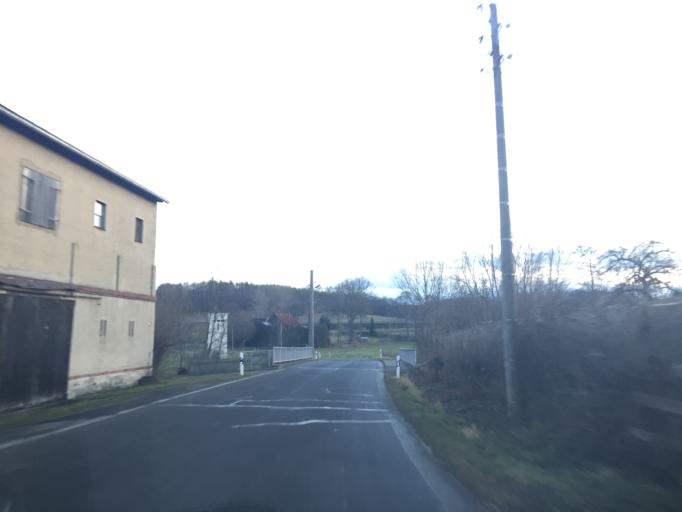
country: DE
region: Thuringia
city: Nobdenitz
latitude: 50.8868
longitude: 12.3054
